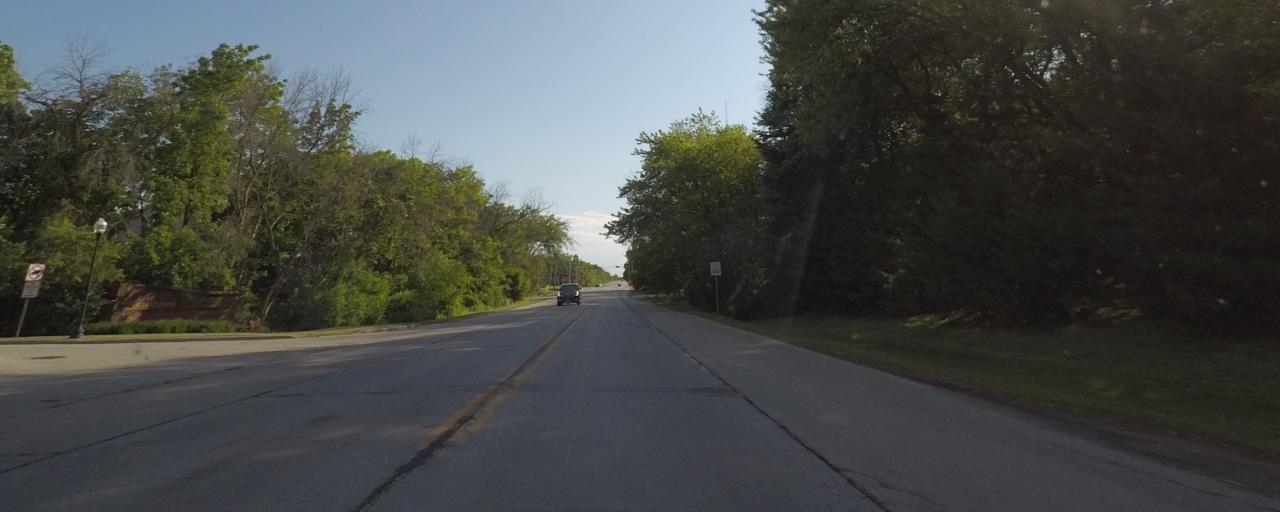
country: US
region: Wisconsin
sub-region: Milwaukee County
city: Hales Corners
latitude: 42.9651
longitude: -88.0670
